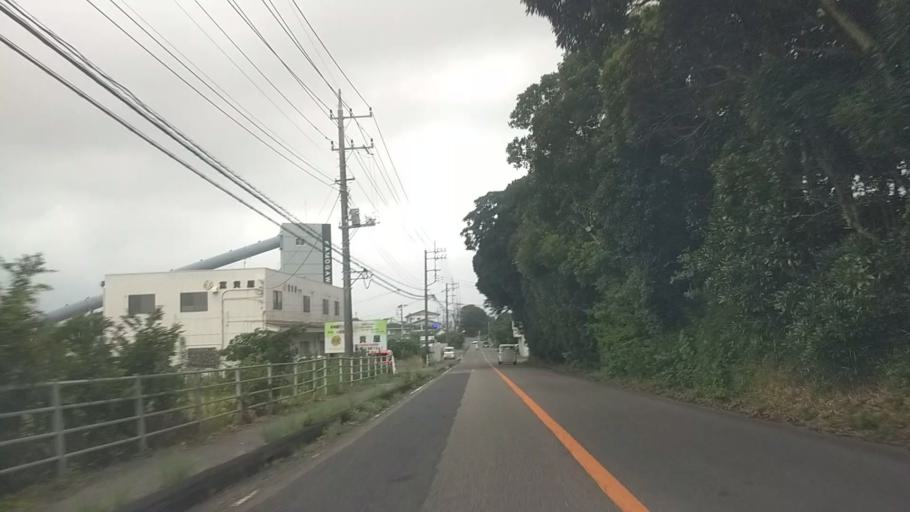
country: JP
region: Chiba
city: Kawaguchi
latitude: 35.1172
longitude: 140.0758
